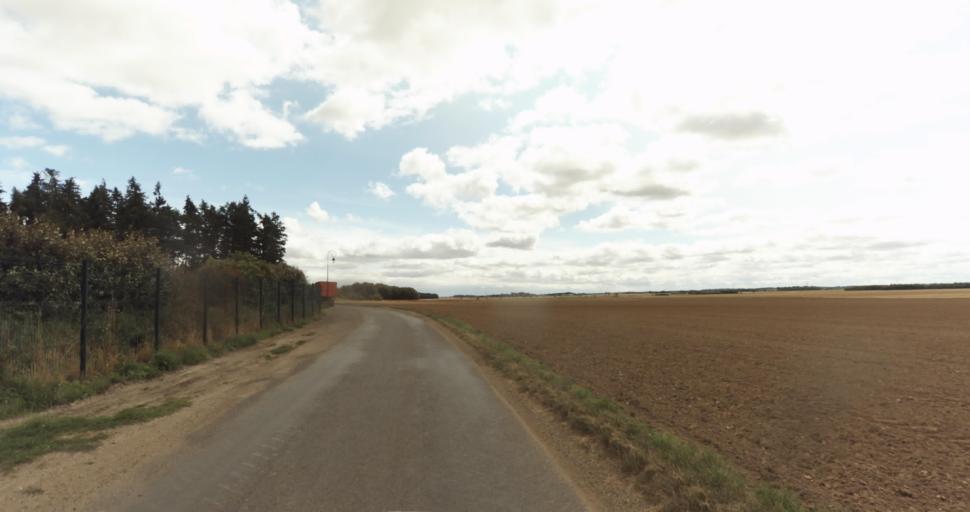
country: FR
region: Haute-Normandie
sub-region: Departement de l'Eure
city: Damville
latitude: 48.8957
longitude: 1.1878
